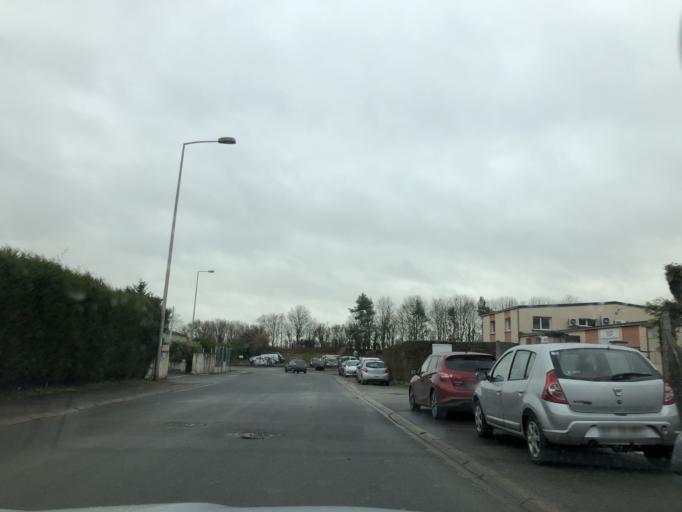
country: FR
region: Lower Normandy
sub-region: Departement du Calvados
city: Giberville
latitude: 49.1688
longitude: -0.2878
